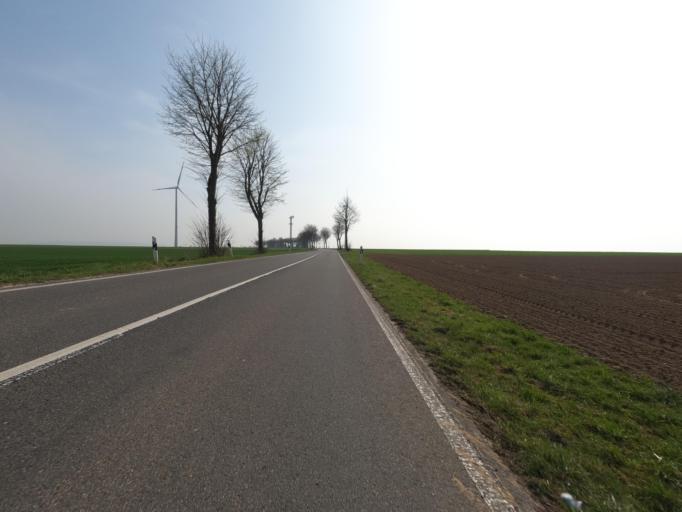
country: DE
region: North Rhine-Westphalia
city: Erkelenz
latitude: 51.0187
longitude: 6.3343
